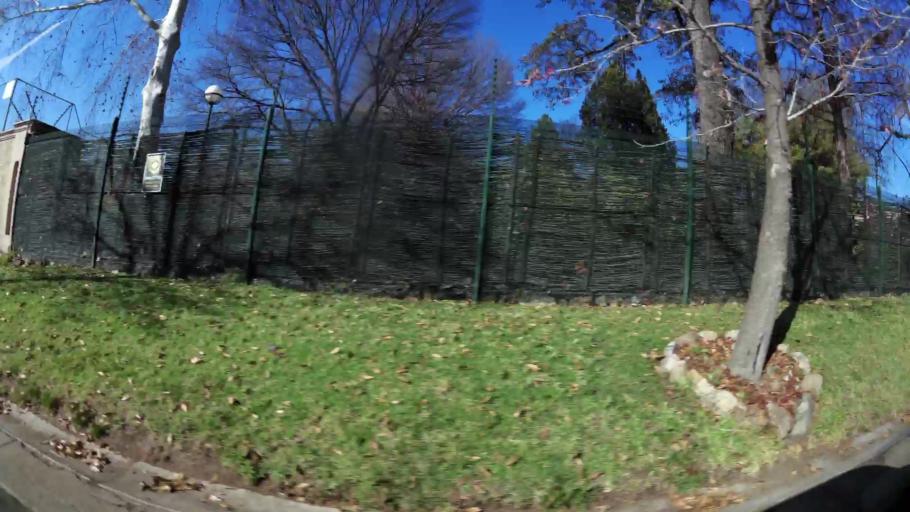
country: ZA
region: Gauteng
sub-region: City of Johannesburg Metropolitan Municipality
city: Midrand
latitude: -26.0618
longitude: 28.0461
